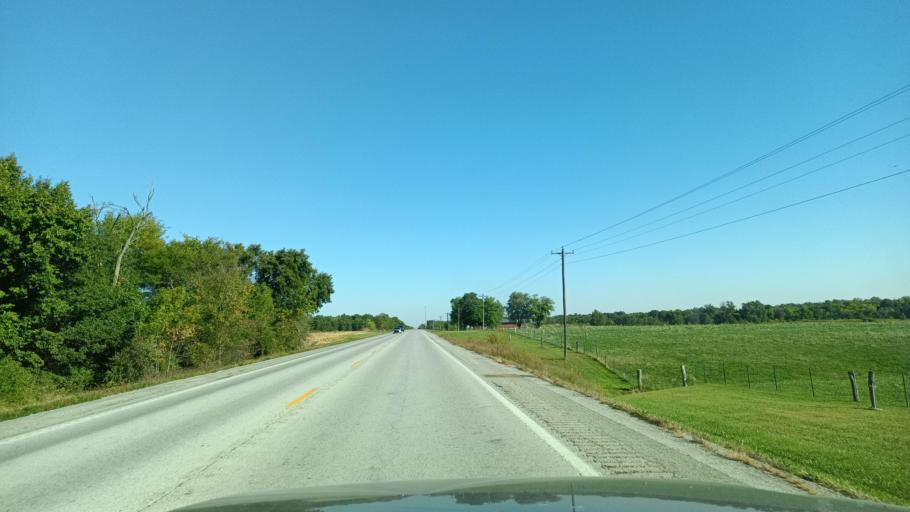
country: US
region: Missouri
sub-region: Audrain County
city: Vandalia
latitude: 39.3799
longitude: -91.6420
